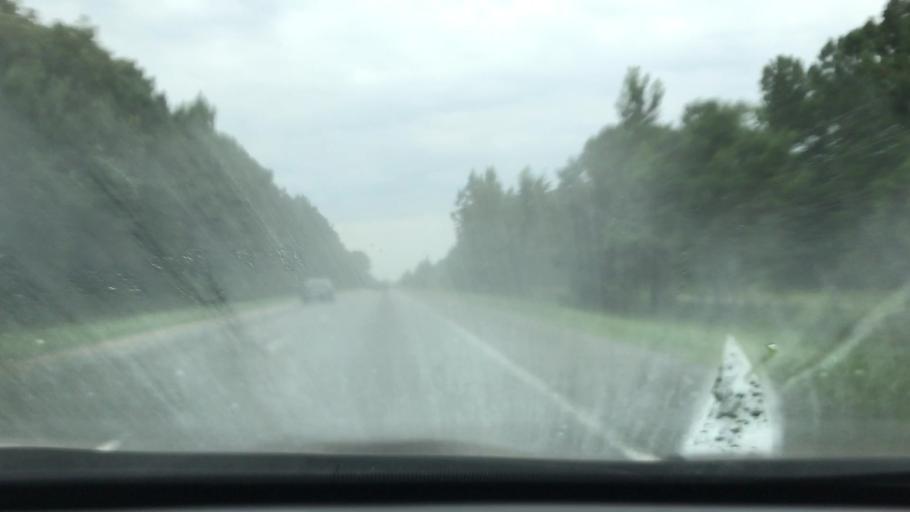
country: US
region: South Carolina
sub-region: Jasper County
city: Ridgeland
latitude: 32.5168
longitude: -80.9651
